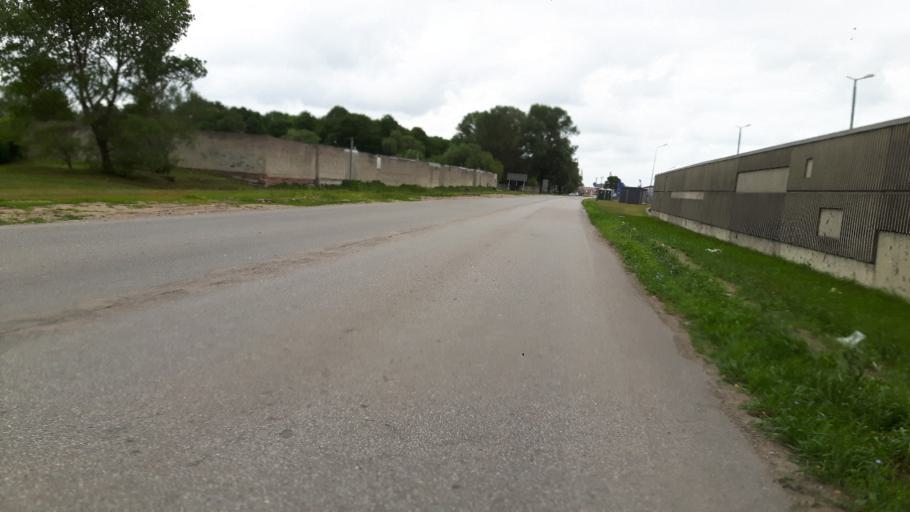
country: LV
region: Liepaja
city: Vec-Liepaja
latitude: 56.5336
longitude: 20.9995
